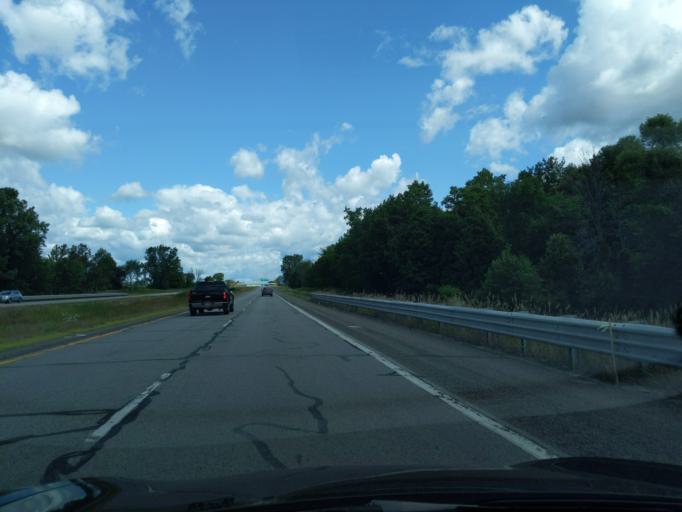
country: US
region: Michigan
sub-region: Clare County
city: Clare
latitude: 43.7769
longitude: -84.7584
